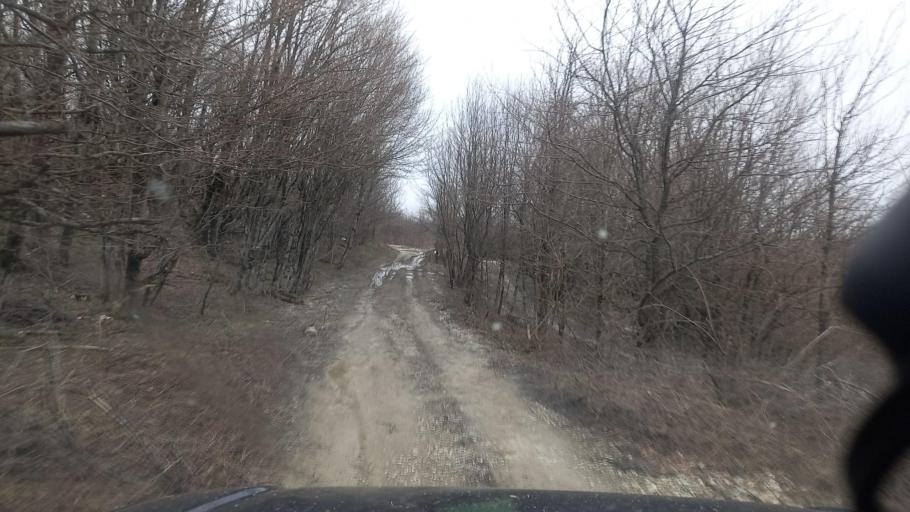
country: RU
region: Krasnodarskiy
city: Pshada
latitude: 44.5955
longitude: 38.3188
